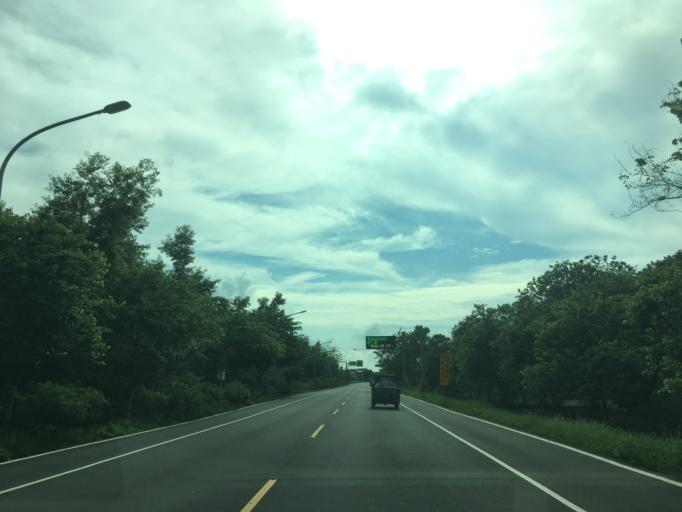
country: TW
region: Taiwan
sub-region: Chiayi
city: Jiayi Shi
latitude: 23.4526
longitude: 120.5615
